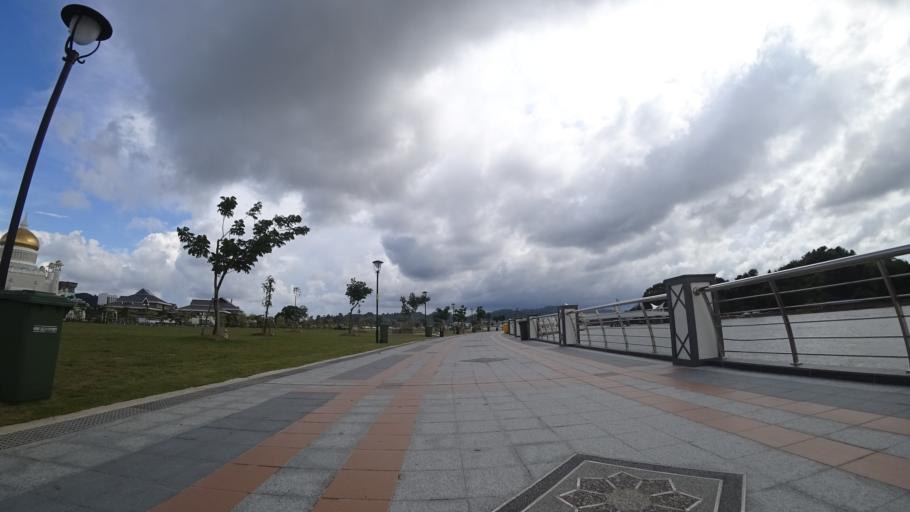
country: BN
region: Brunei and Muara
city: Bandar Seri Begawan
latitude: 4.8903
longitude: 114.9372
